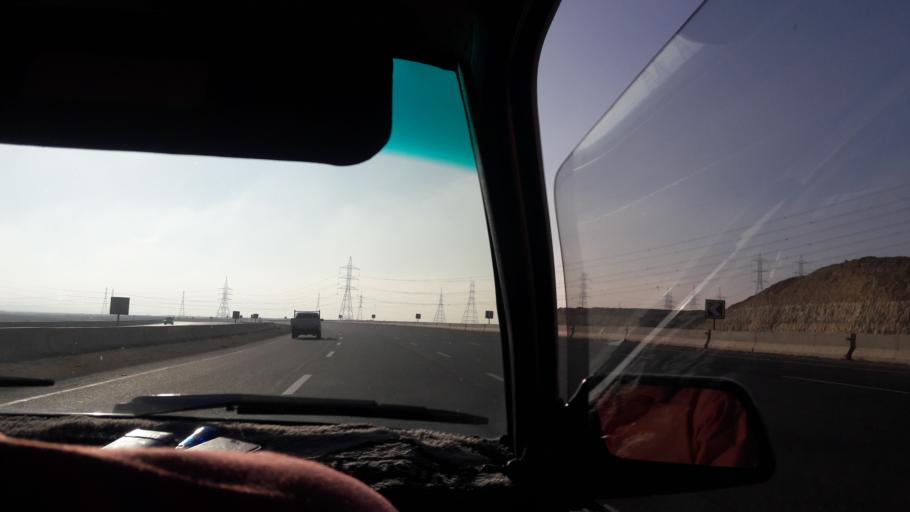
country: EG
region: Muhafazat al Qahirah
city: Halwan
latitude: 29.9042
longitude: 31.4957
